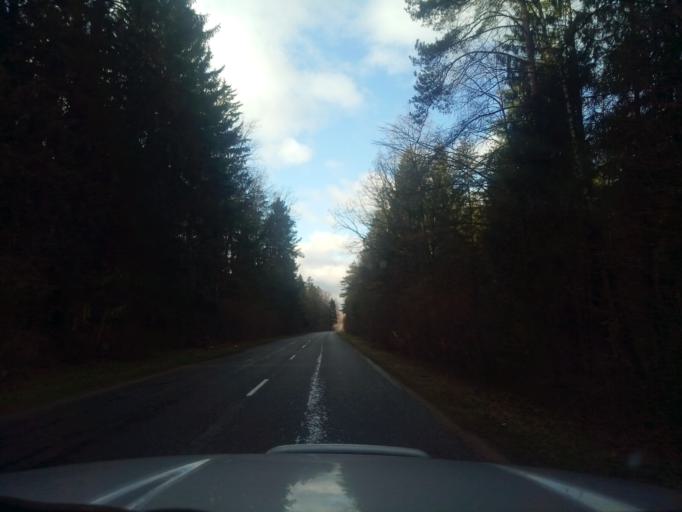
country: BY
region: Minsk
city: Kapyl'
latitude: 53.1751
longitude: 26.9890
